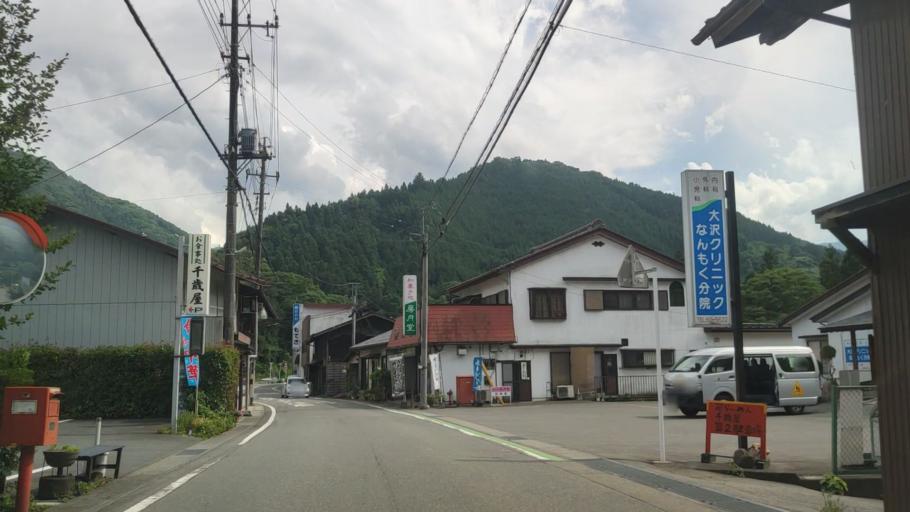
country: JP
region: Gunma
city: Tomioka
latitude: 36.1684
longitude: 138.7283
